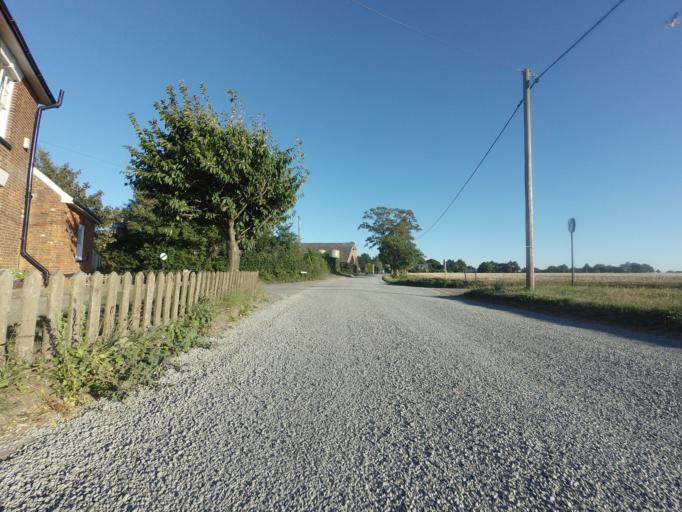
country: GB
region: England
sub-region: Kent
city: Herne Bay
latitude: 51.3364
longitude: 1.1906
